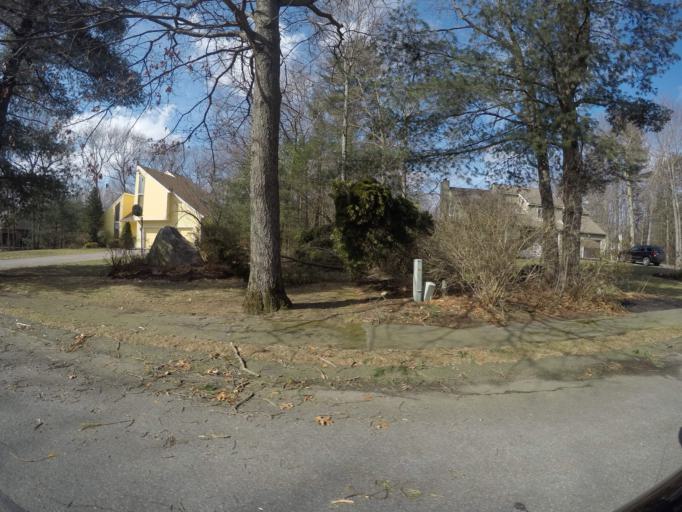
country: US
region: Massachusetts
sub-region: Bristol County
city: Easton
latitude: 42.0122
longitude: -71.1426
